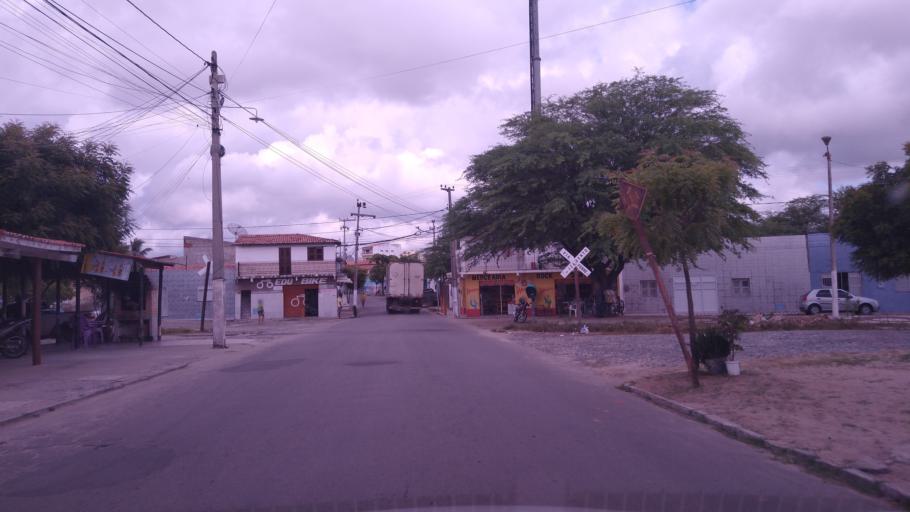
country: BR
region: Ceara
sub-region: Quixada
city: Quixada
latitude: -4.9637
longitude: -39.0134
